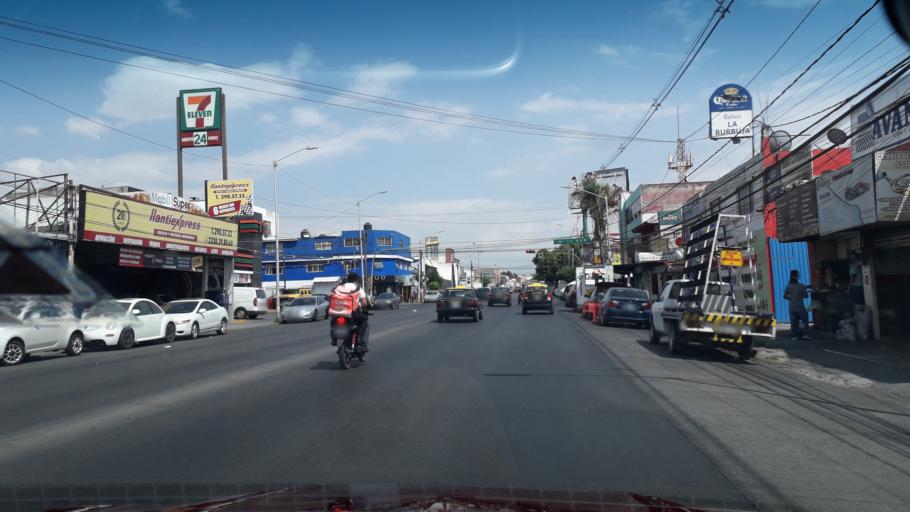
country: MX
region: Puebla
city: Puebla
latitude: 19.0413
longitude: -98.2223
